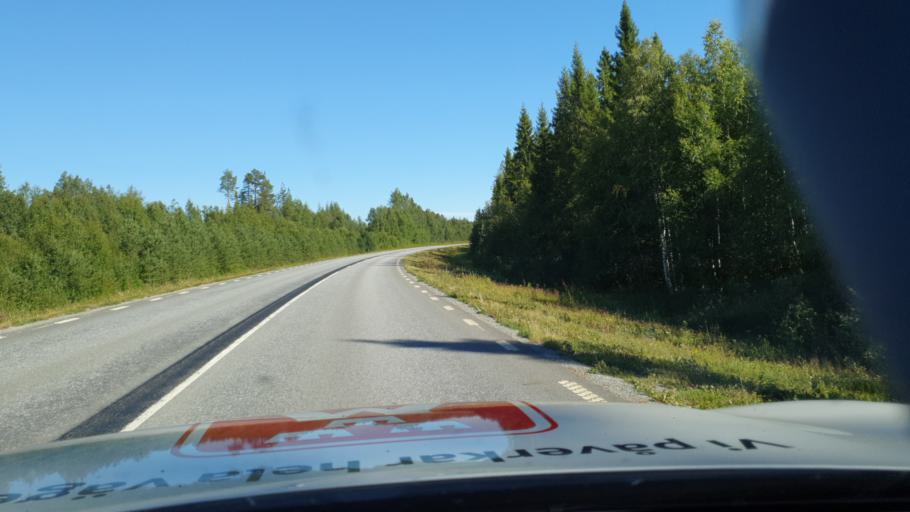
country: SE
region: Vaesterbotten
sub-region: Dorotea Kommun
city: Dorotea
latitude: 64.3408
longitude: 16.6433
